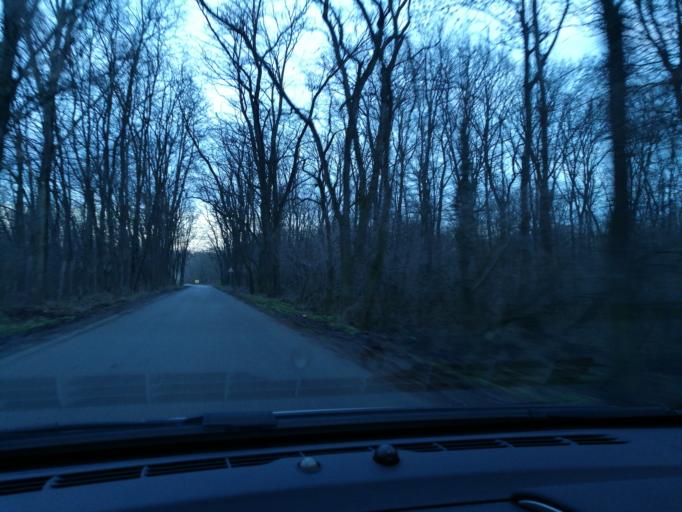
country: HU
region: Szabolcs-Szatmar-Bereg
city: Nyiregyhaza
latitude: 47.9830
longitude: 21.7059
